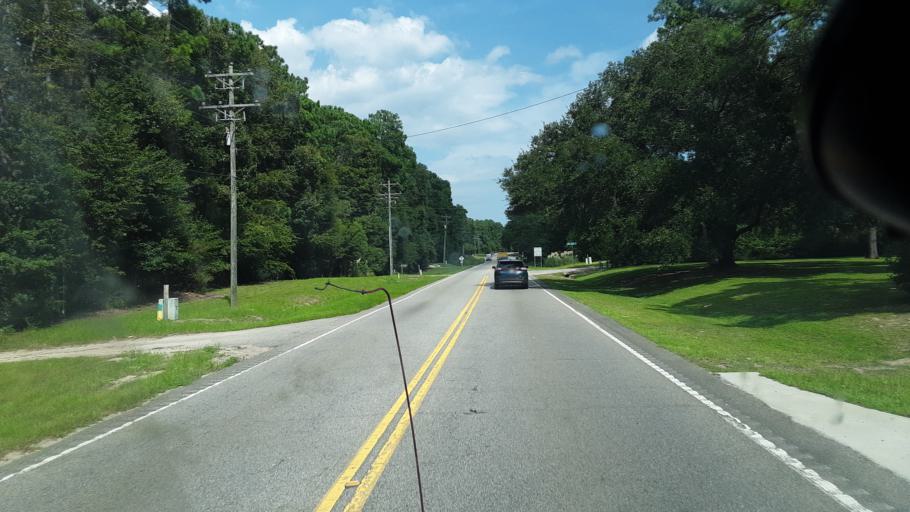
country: US
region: South Carolina
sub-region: Horry County
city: Red Hill
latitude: 33.8212
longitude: -78.9307
